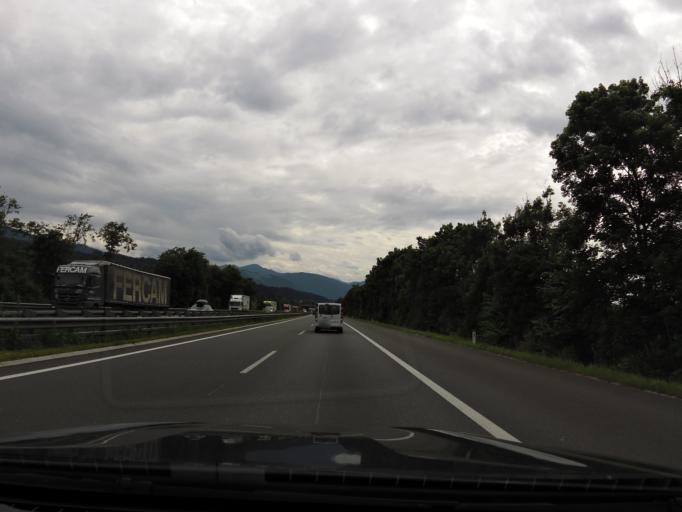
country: AT
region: Tyrol
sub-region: Politischer Bezirk Kufstein
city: Schwoich
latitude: 47.5490
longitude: 12.1198
